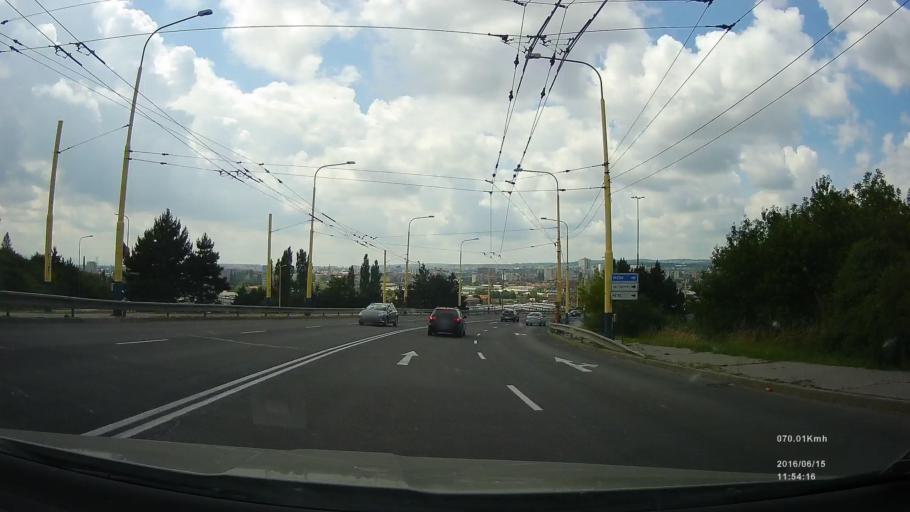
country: SK
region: Kosicky
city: Kosice
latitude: 48.7426
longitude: 21.2730
